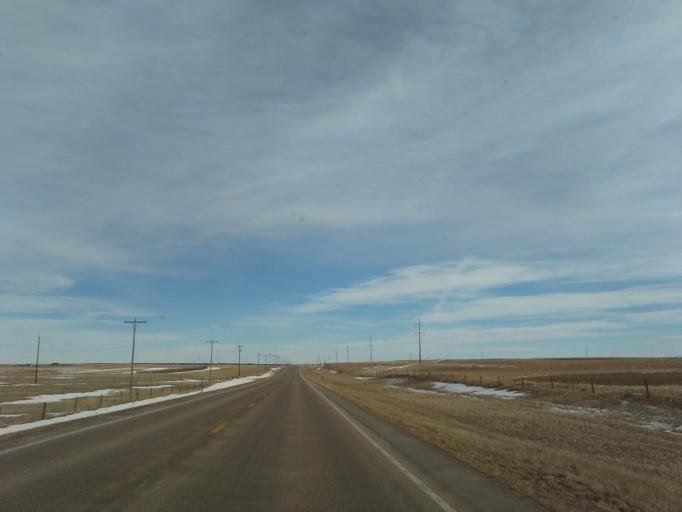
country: US
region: Wyoming
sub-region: Laramie County
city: Ranchettes
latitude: 41.4038
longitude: -104.4569
